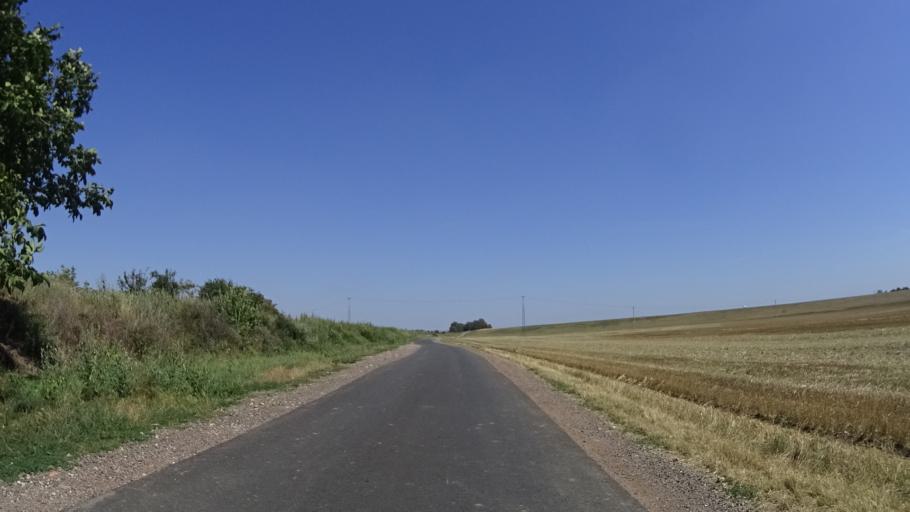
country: CZ
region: South Moravian
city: Petrov
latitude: 48.8811
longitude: 17.2830
